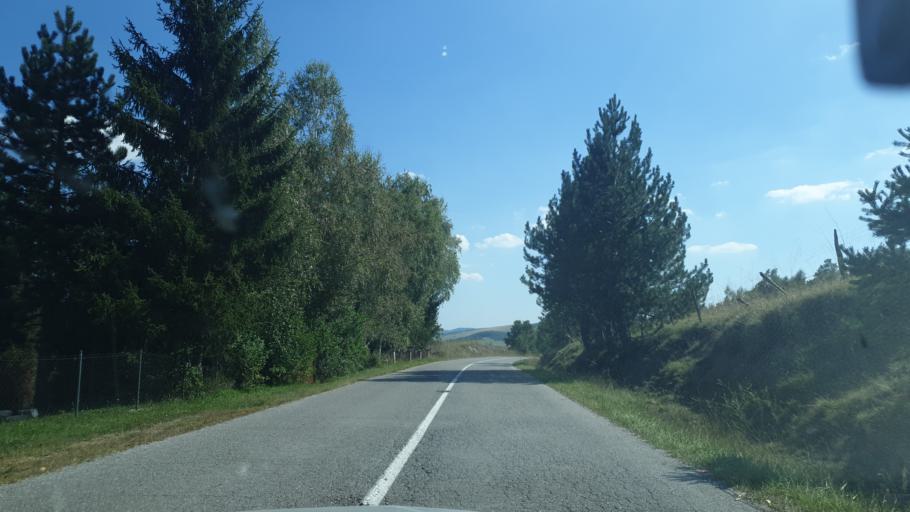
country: RS
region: Central Serbia
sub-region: Zlatiborski Okrug
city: Kosjeric
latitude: 44.0683
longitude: 20.0201
